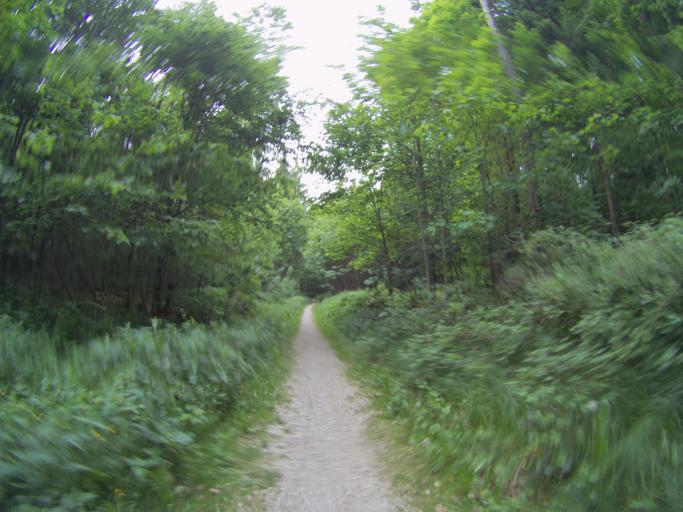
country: DE
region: Bavaria
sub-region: Upper Bavaria
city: Freising
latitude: 48.4142
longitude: 11.7418
